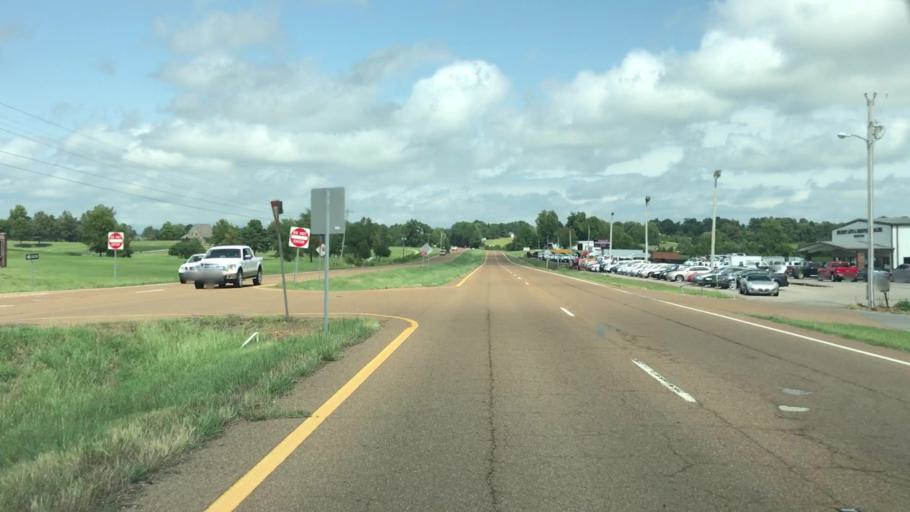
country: US
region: Tennessee
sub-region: Obion County
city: Englewood
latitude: 36.3504
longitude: -89.1447
